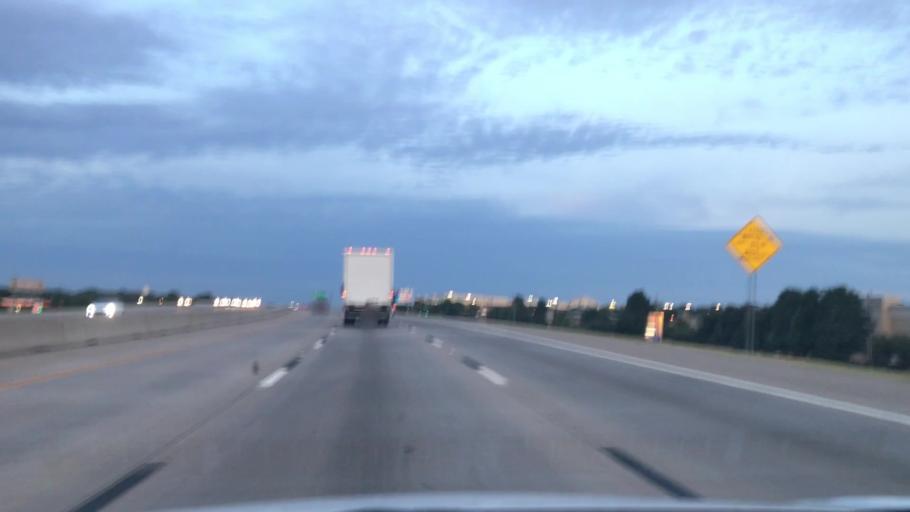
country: US
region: Texas
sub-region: Tarrant County
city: Southlake
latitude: 32.9434
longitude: -97.1204
